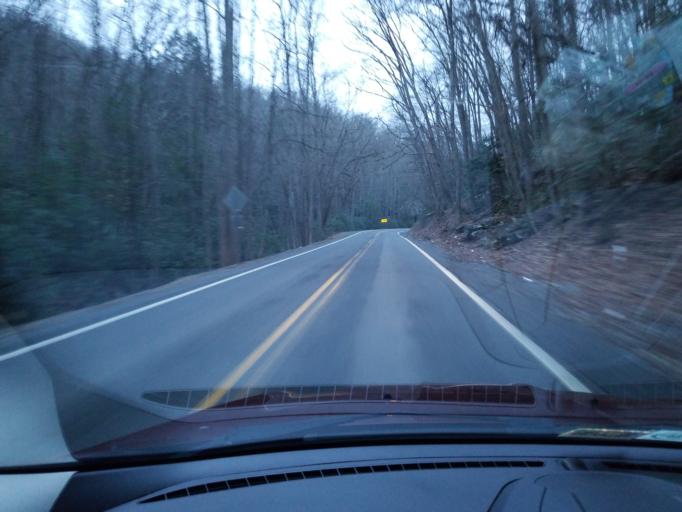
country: US
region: West Virginia
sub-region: Greenbrier County
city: Ronceverte
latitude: 37.7444
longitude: -80.4079
